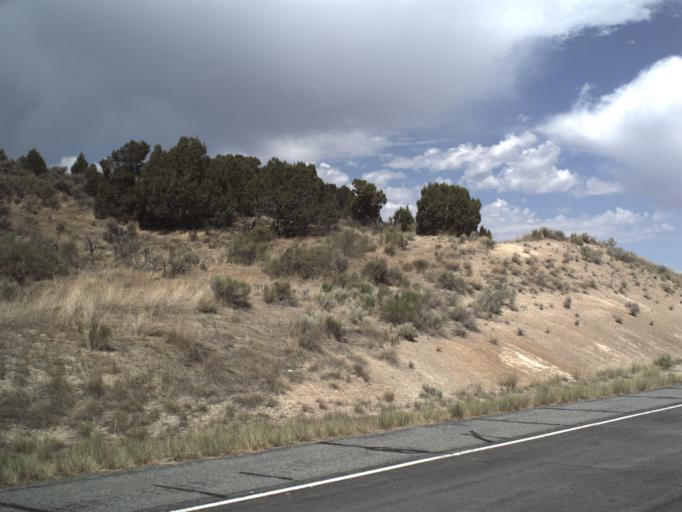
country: US
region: Utah
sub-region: Utah County
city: Eagle Mountain
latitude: 39.9942
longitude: -112.2699
